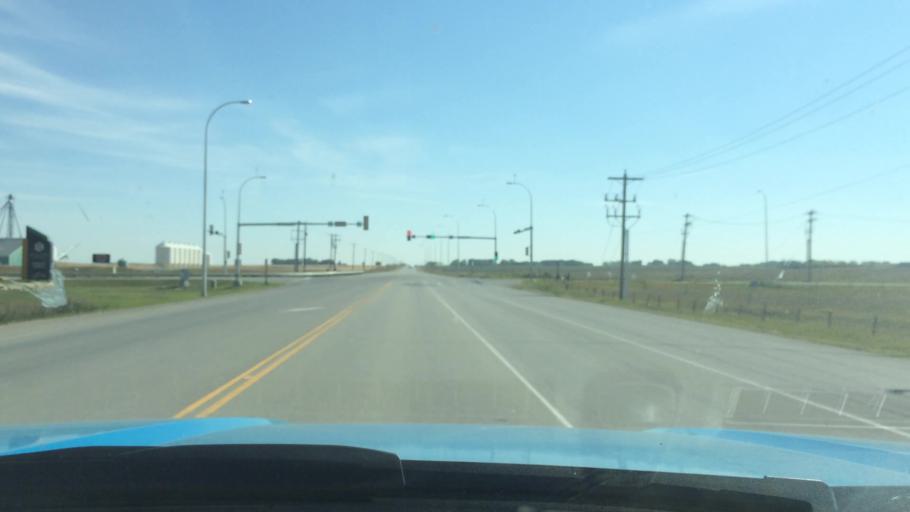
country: CA
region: Alberta
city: Airdrie
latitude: 51.2126
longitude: -113.9369
